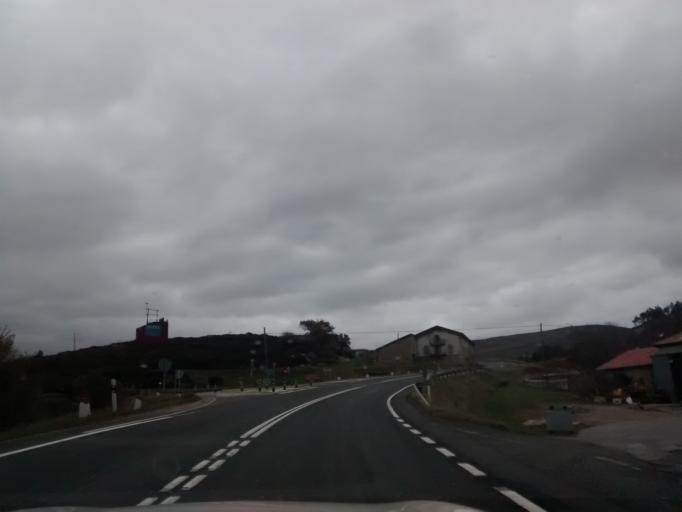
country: ES
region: Castille and Leon
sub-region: Provincia de Burgos
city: Arija
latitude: 43.0282
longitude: -3.8630
